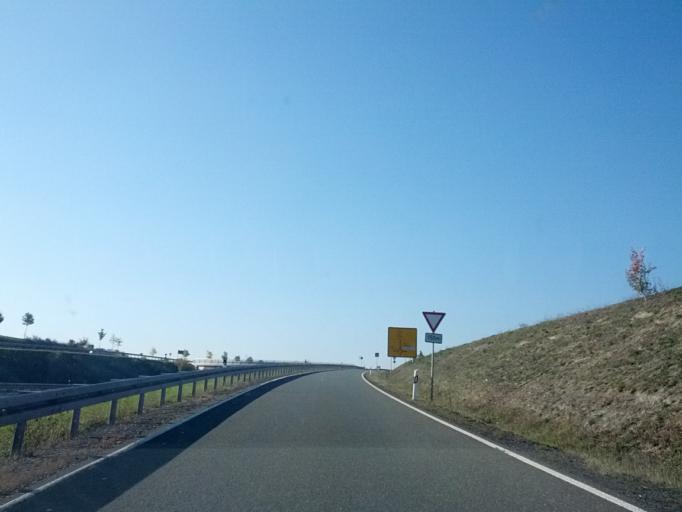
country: DE
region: Thuringia
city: Schwaara
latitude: 50.8986
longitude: 12.1219
